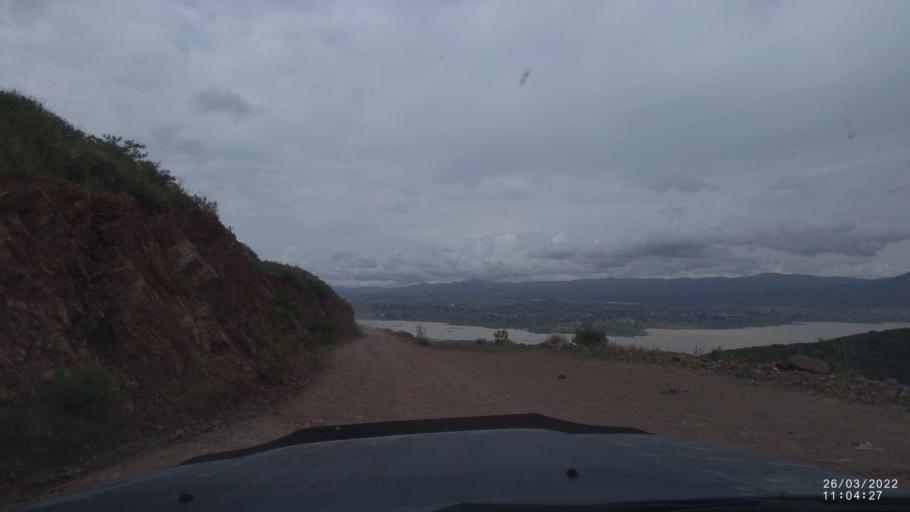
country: BO
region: Cochabamba
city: Tarata
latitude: -17.5295
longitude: -66.0261
